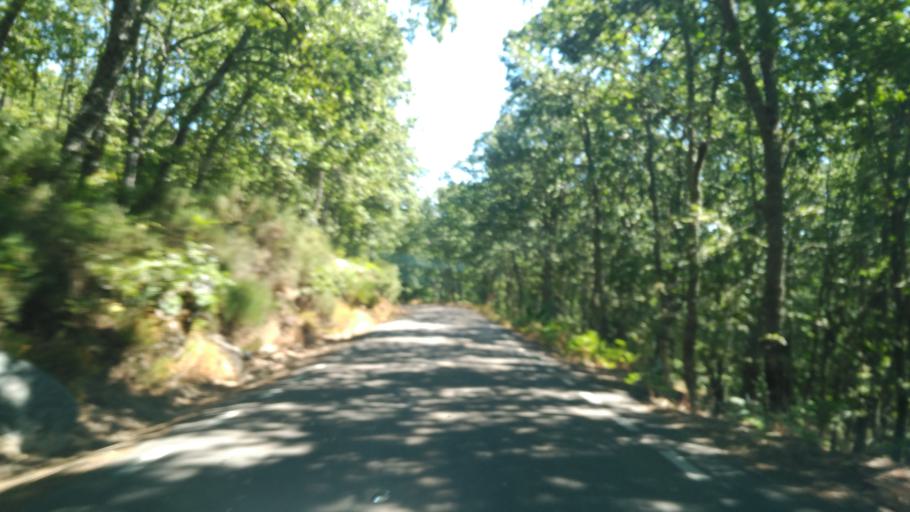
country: ES
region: Castille and Leon
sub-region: Provincia de Salamanca
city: Nava de Francia
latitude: 40.5245
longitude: -6.0929
